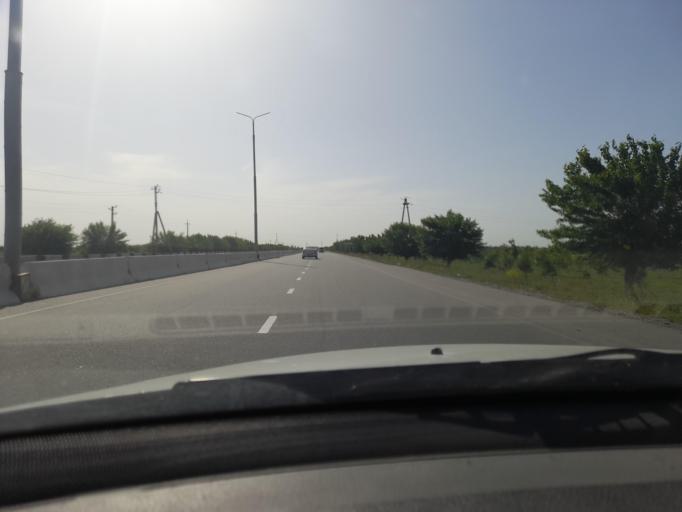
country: UZ
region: Samarqand
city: Ishtixon
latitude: 39.9567
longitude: 66.4739
